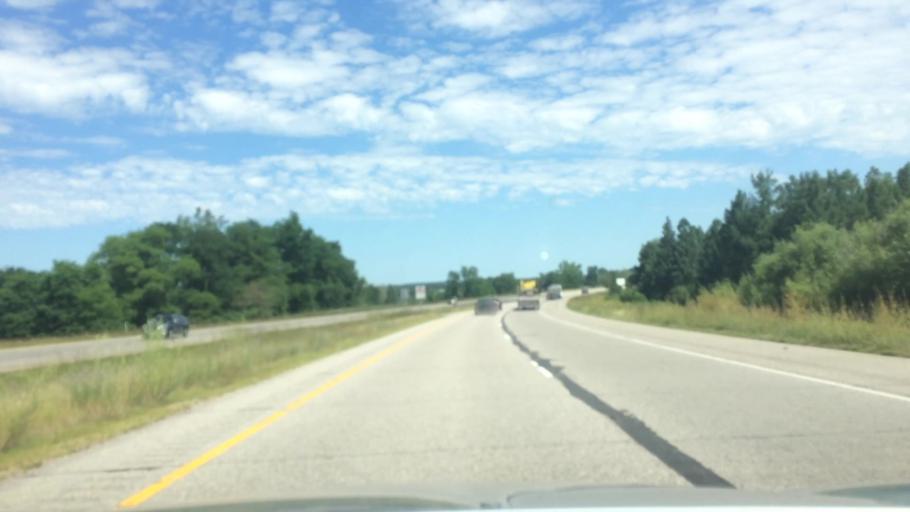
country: US
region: Wisconsin
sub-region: Marquette County
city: Westfield
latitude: 43.7319
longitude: -89.4847
